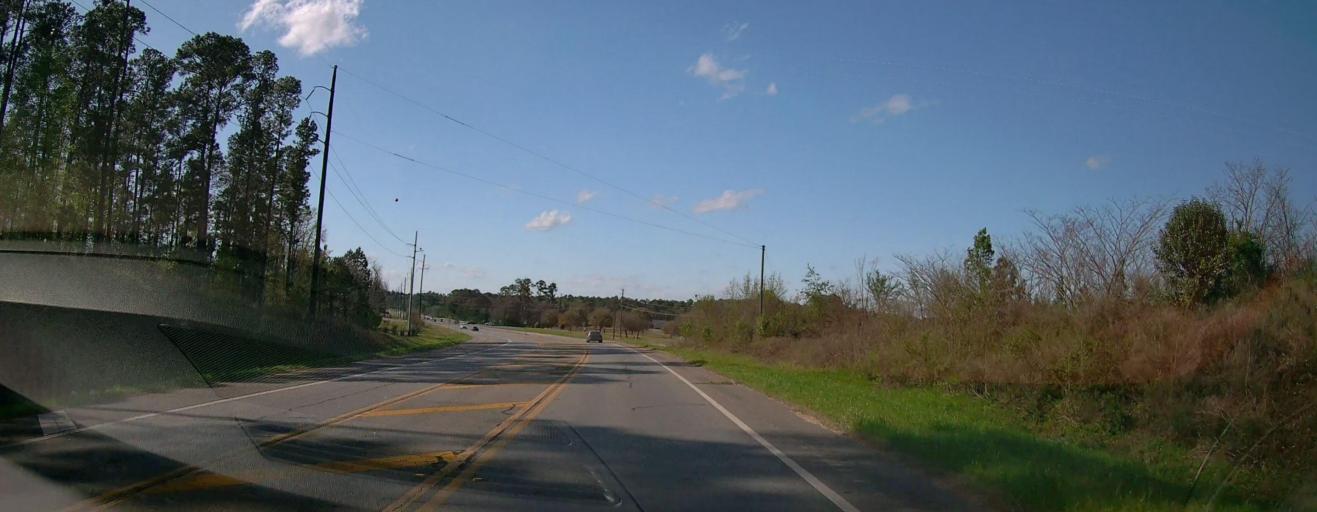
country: US
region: Georgia
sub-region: Baldwin County
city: Milledgeville
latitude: 33.0877
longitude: -83.2469
